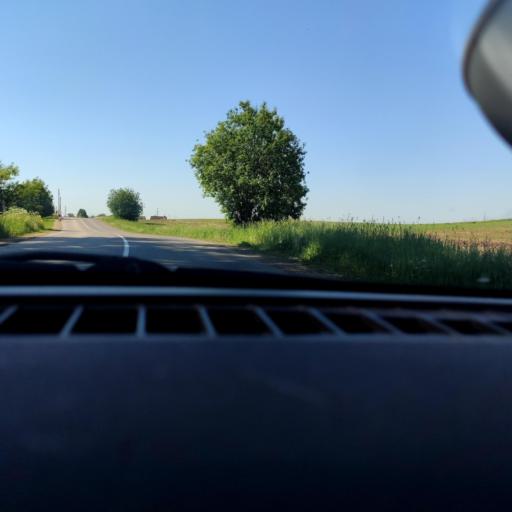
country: RU
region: Perm
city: Ferma
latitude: 57.9222
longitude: 56.3286
